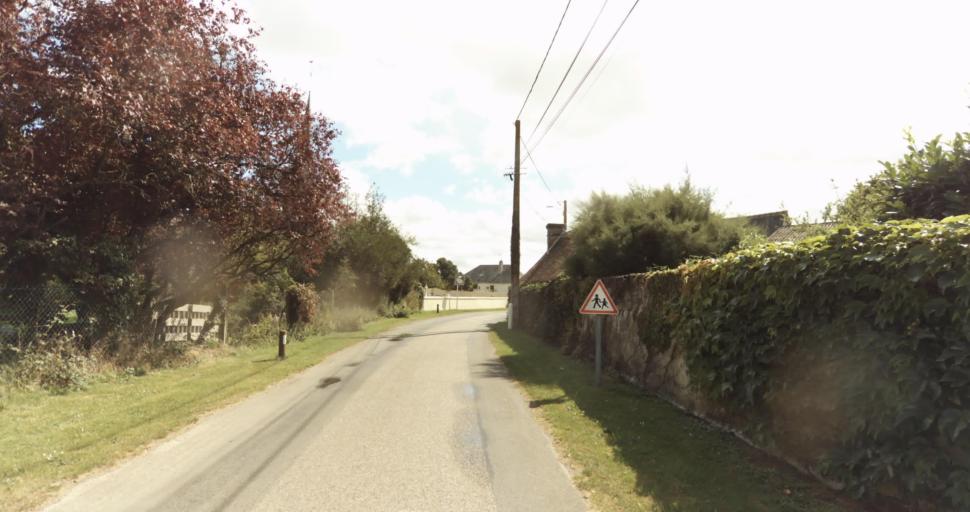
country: FR
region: Haute-Normandie
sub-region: Departement de l'Eure
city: Nonancourt
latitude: 48.8449
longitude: 1.1635
